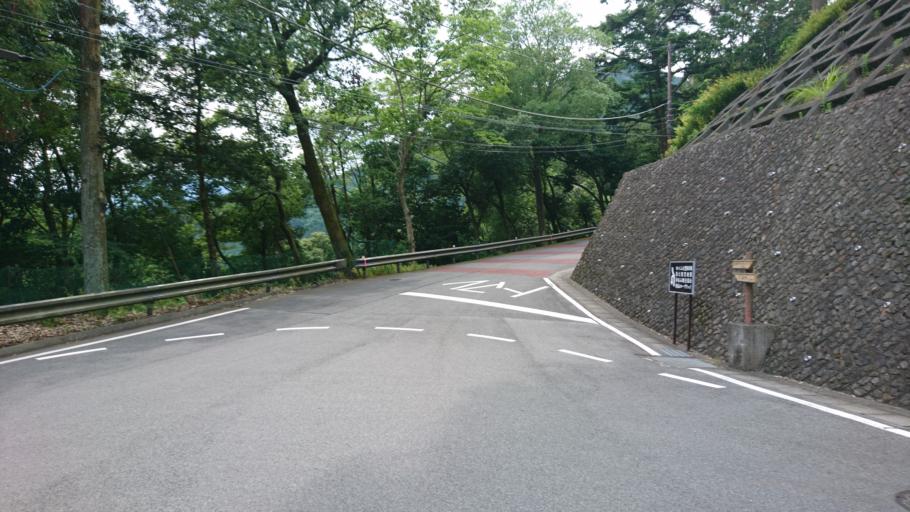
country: JP
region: Shizuoka
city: Fujinomiya
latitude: 35.3809
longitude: 138.4286
